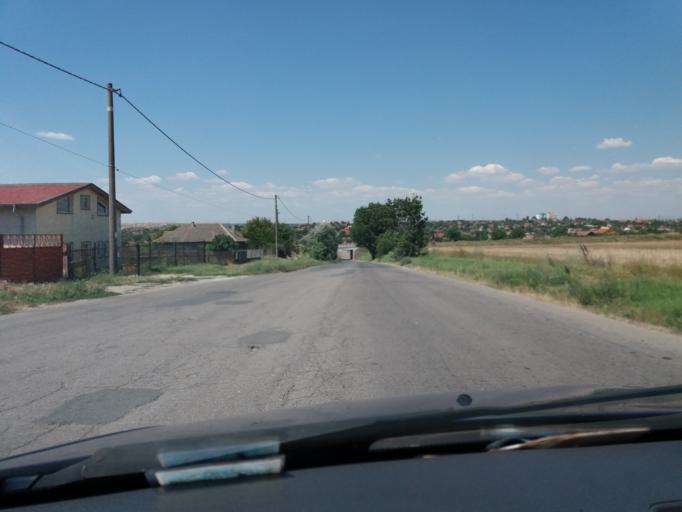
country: RO
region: Constanta
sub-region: Comuna Lumina
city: Lumina
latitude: 44.2852
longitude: 28.5773
